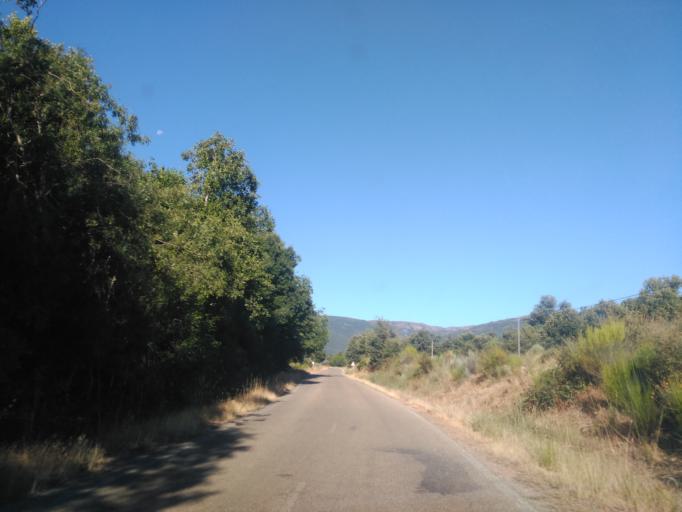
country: ES
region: Castille and Leon
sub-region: Provincia de Zamora
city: Cobreros
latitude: 42.0871
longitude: -6.6851
